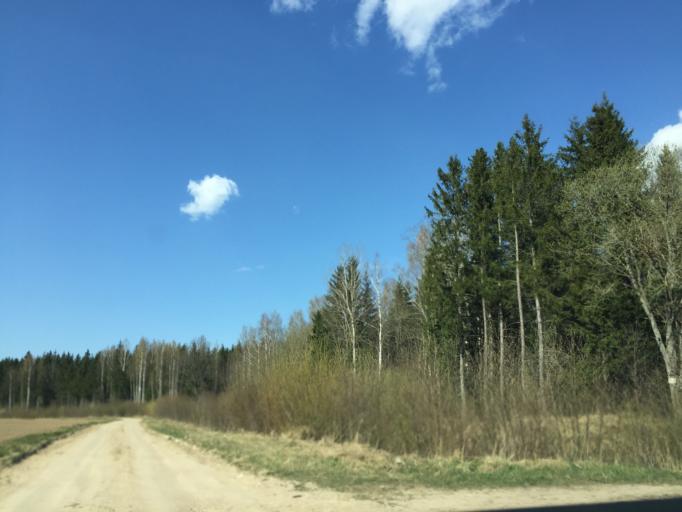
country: LV
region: Lielvarde
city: Lielvarde
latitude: 56.8380
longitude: 24.7972
